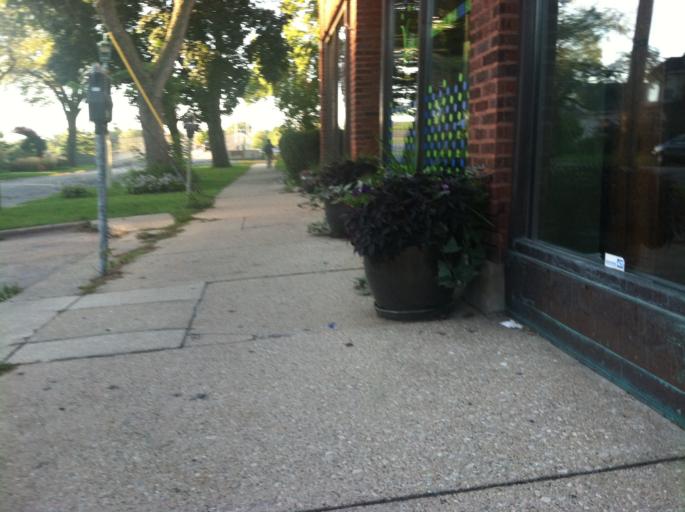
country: US
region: Illinois
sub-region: Cook County
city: Oak Park
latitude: 41.8724
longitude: -87.7793
